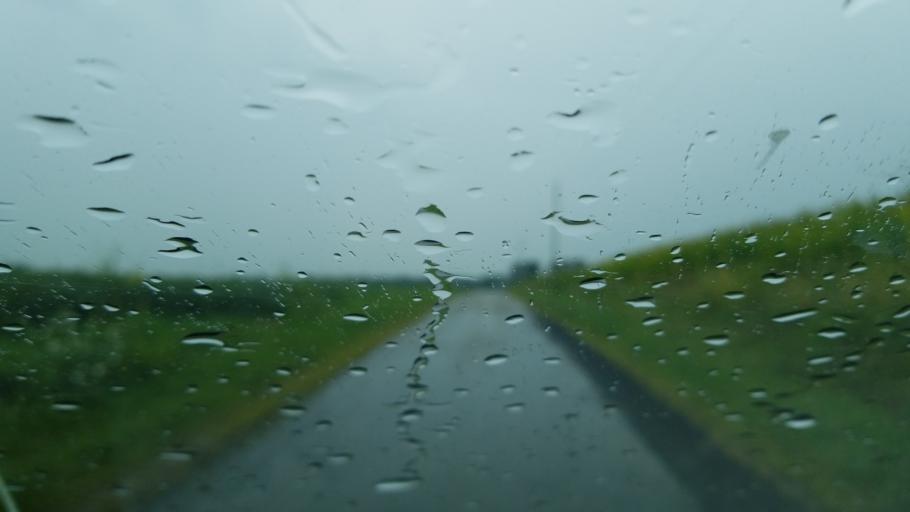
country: US
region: Ohio
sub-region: Richland County
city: Shelby
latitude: 40.9311
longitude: -82.7724
